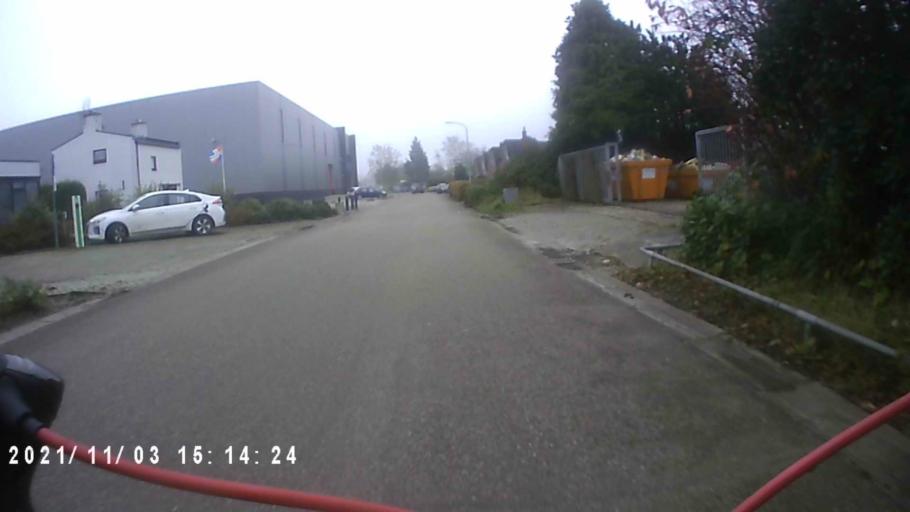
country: NL
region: Groningen
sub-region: Gemeente Leek
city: Leek
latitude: 53.1690
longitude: 6.3565
